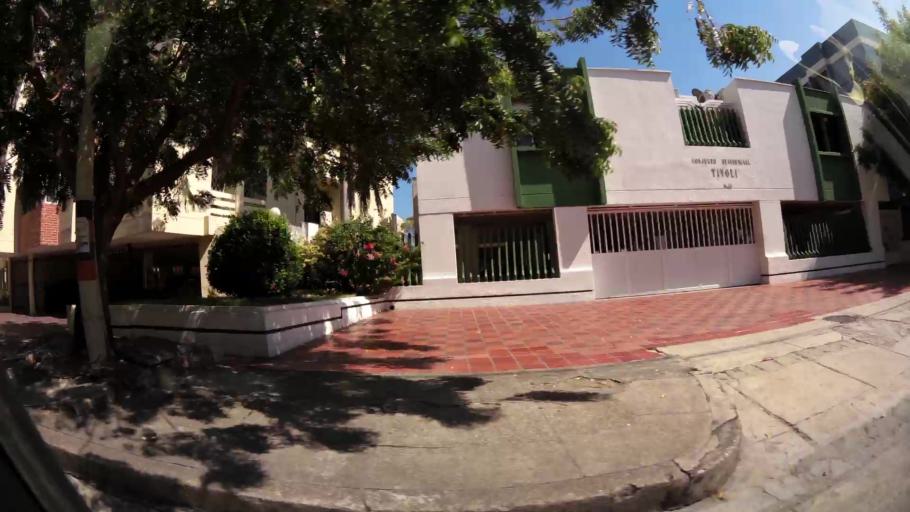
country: CO
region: Atlantico
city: Barranquilla
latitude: 11.0151
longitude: -74.8167
